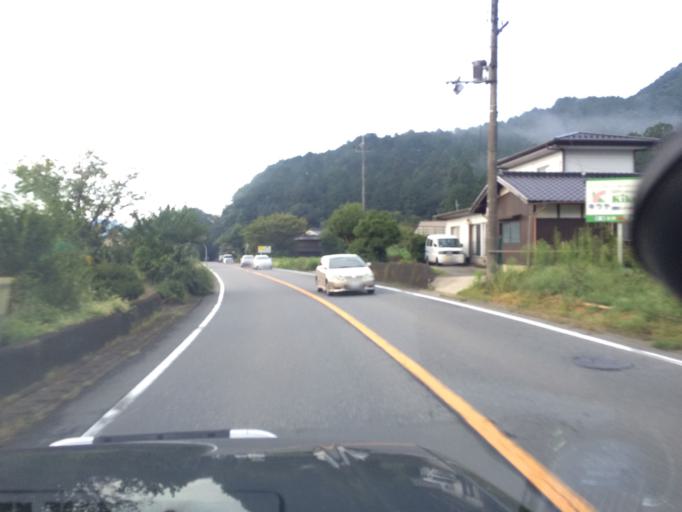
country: JP
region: Hyogo
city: Nishiwaki
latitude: 35.1326
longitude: 135.0165
